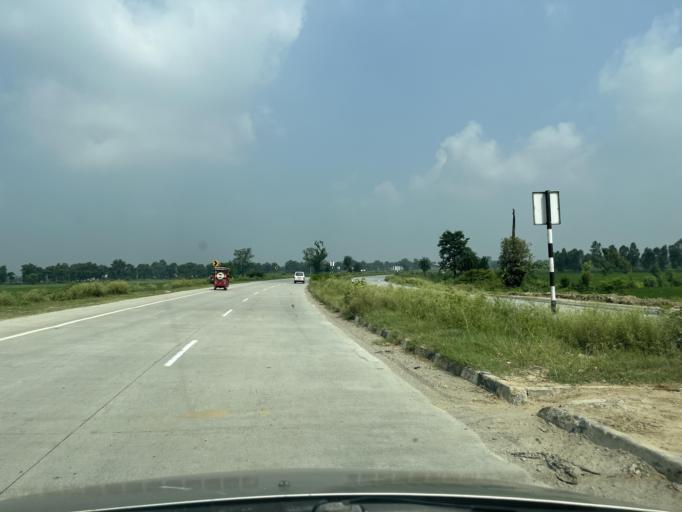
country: IN
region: Uttarakhand
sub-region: Udham Singh Nagar
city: Kashipur
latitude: 29.1769
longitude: 78.9404
